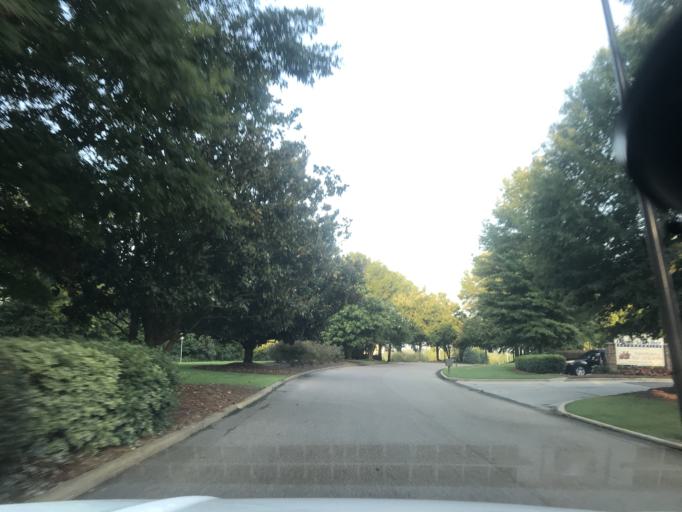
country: US
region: Alabama
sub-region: Montgomery County
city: Pike Road
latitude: 32.3681
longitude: -86.1695
